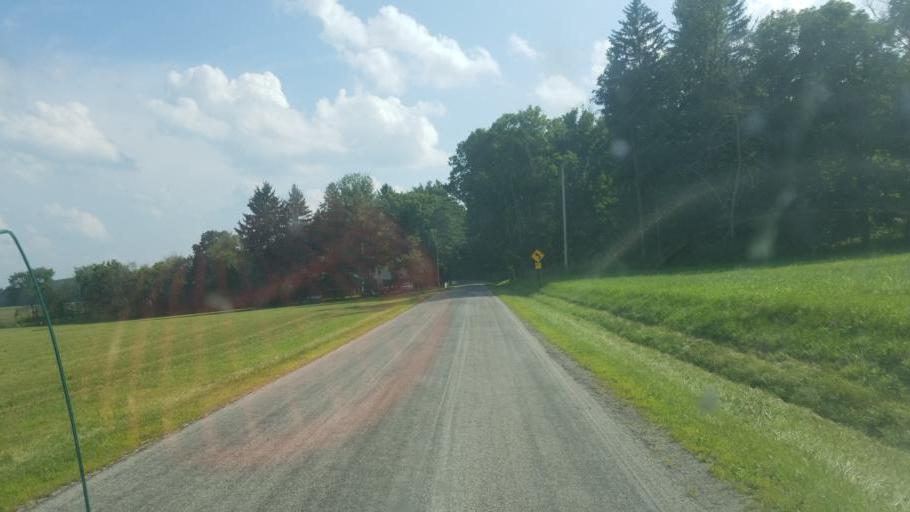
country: US
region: Ohio
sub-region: Wayne County
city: West Salem
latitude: 40.9560
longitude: -82.0345
